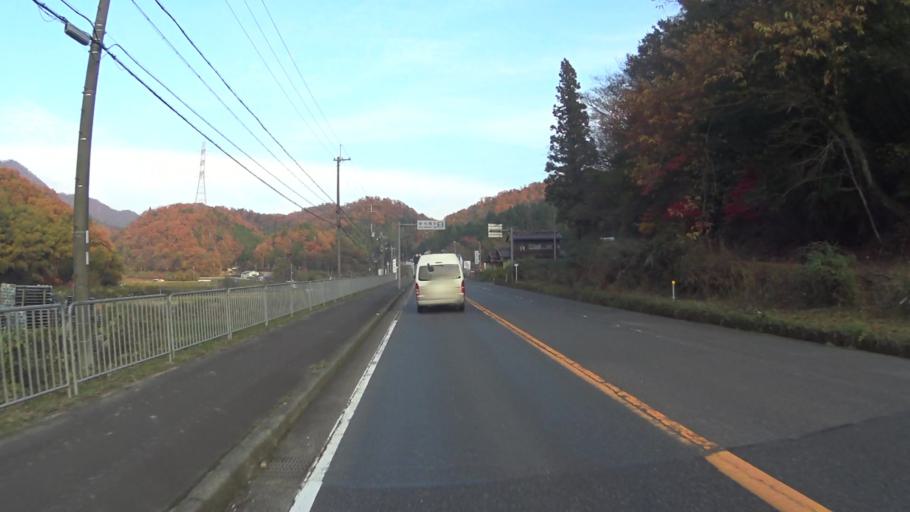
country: JP
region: Kyoto
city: Maizuru
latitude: 35.4860
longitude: 135.4596
